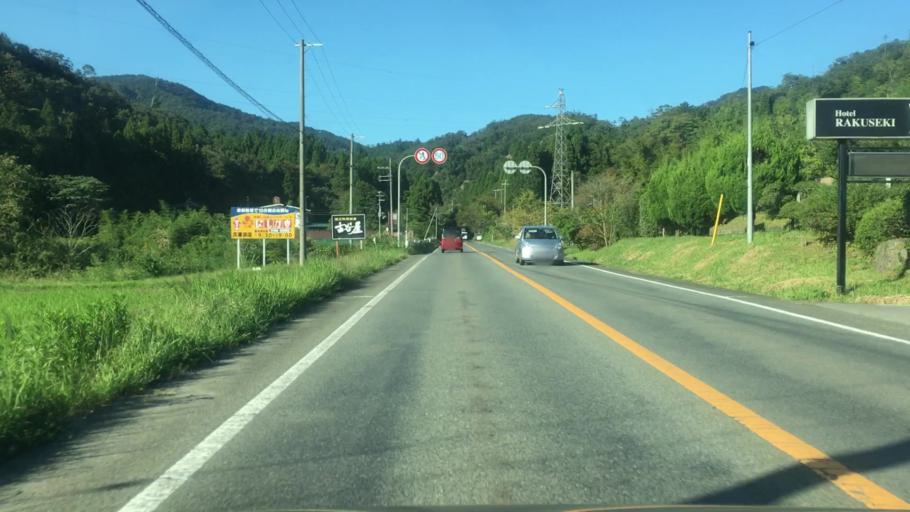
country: JP
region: Hyogo
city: Toyooka
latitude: 35.5615
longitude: 134.8517
